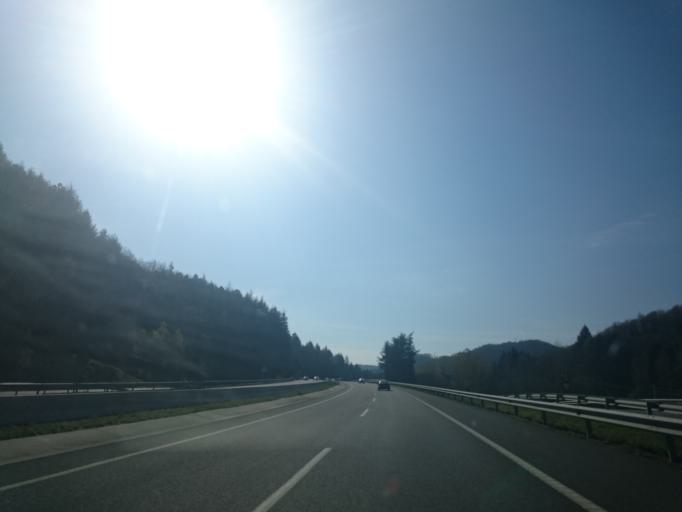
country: ES
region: Catalonia
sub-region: Provincia de Girona
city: Viladrau
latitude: 41.8752
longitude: 2.4028
